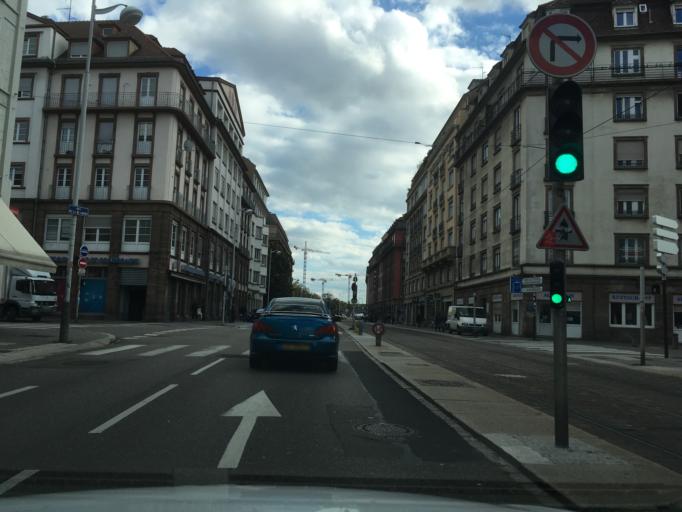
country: FR
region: Alsace
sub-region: Departement du Bas-Rhin
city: Strasbourg
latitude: 48.5774
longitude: 7.7515
